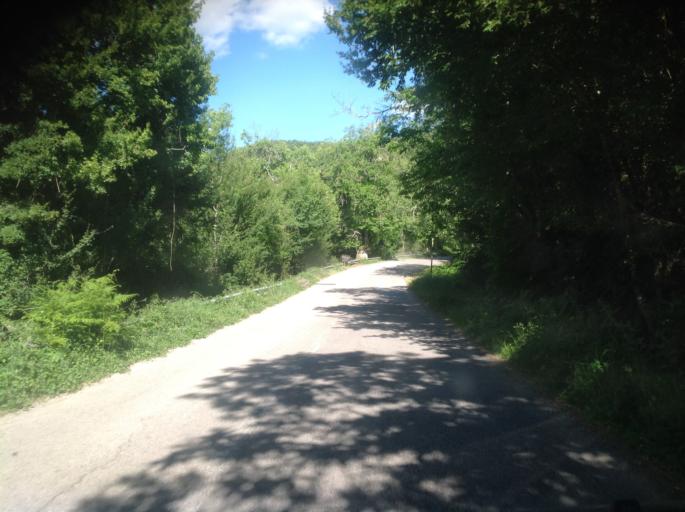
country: IT
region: Umbria
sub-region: Provincia di Terni
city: Stroncone
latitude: 42.4874
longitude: 12.6920
